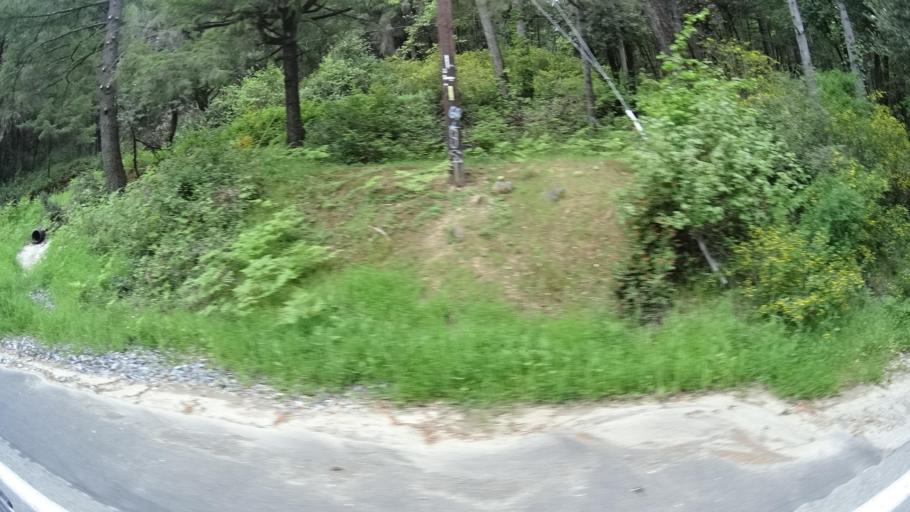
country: US
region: California
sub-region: Humboldt County
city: Redway
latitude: 40.1200
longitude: -123.8844
